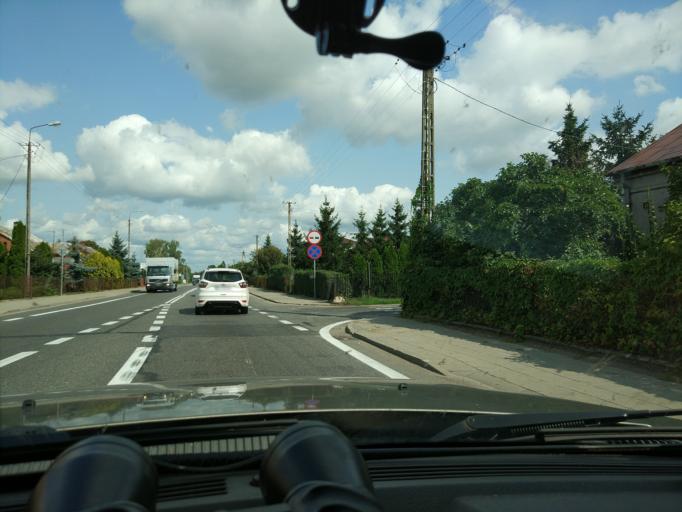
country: PL
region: Masovian Voivodeship
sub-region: Powiat mlawski
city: Wisniewo
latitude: 53.0641
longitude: 20.3479
